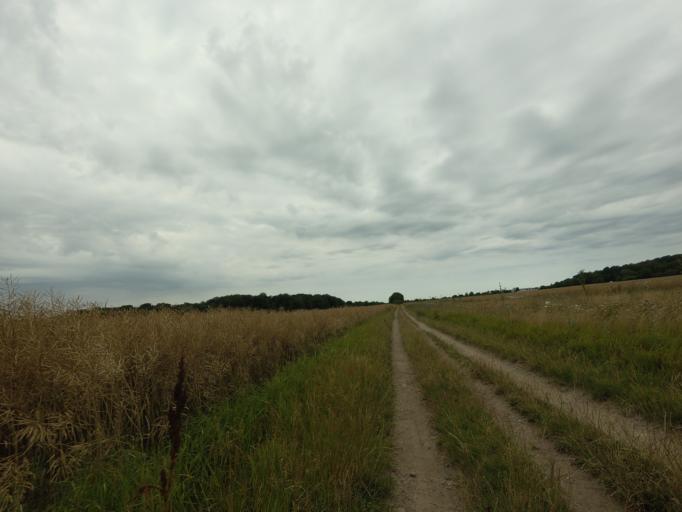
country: SE
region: Skane
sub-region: Helsingborg
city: Helsingborg
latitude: 56.0886
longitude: 12.6757
